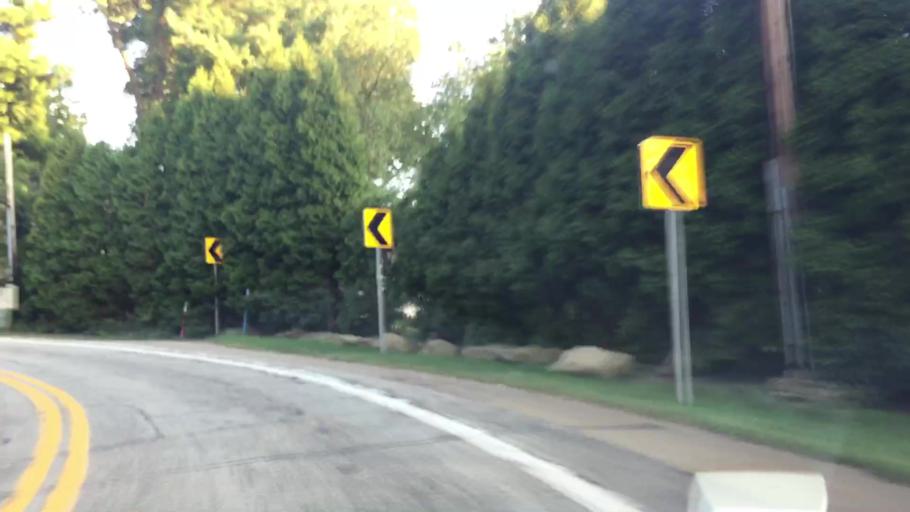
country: US
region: Pennsylvania
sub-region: Allegheny County
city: West View
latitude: 40.5259
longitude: -80.0368
